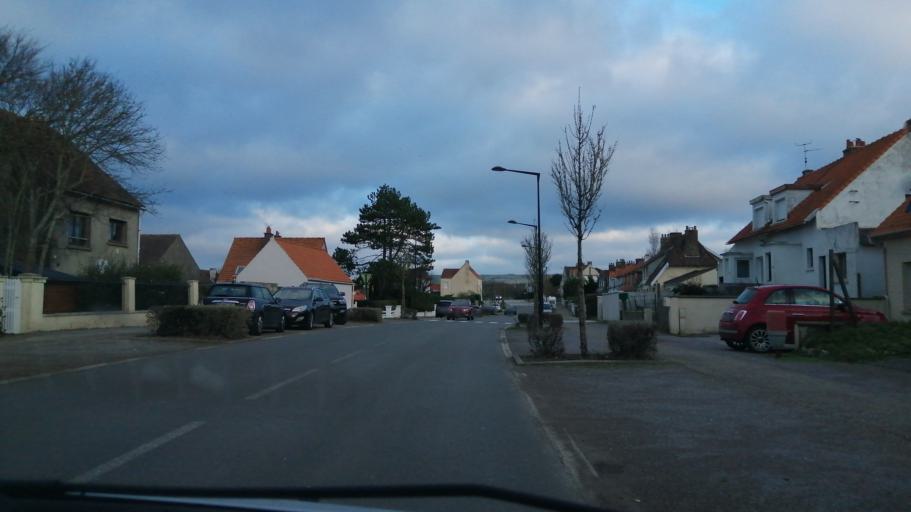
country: FR
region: Nord-Pas-de-Calais
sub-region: Departement du Pas-de-Calais
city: Wissant
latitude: 50.8831
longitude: 1.6612
